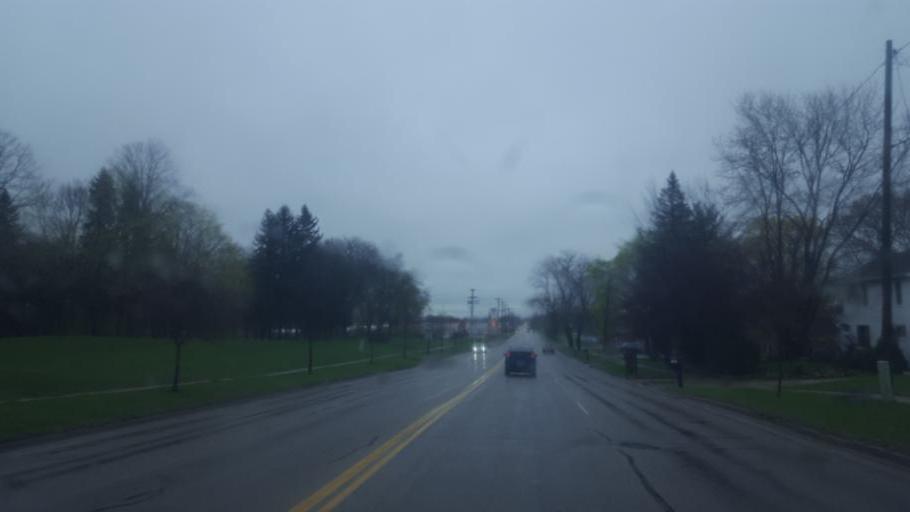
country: US
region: Michigan
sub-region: Isabella County
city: Mount Pleasant
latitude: 43.6117
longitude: -84.7903
